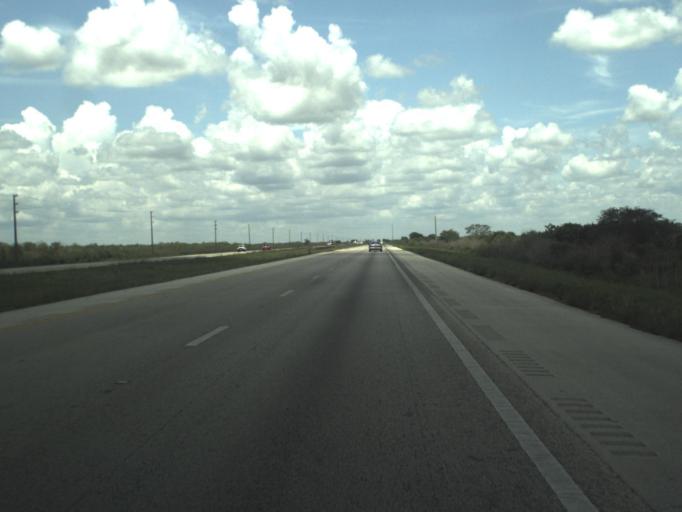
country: US
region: Florida
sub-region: Broward County
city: Weston
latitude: 26.1536
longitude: -80.7447
